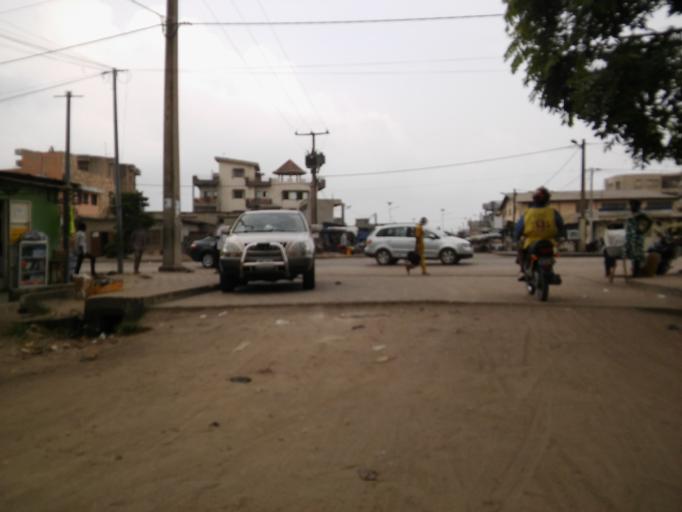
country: BJ
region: Littoral
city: Cotonou
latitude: 6.3890
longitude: 2.3729
